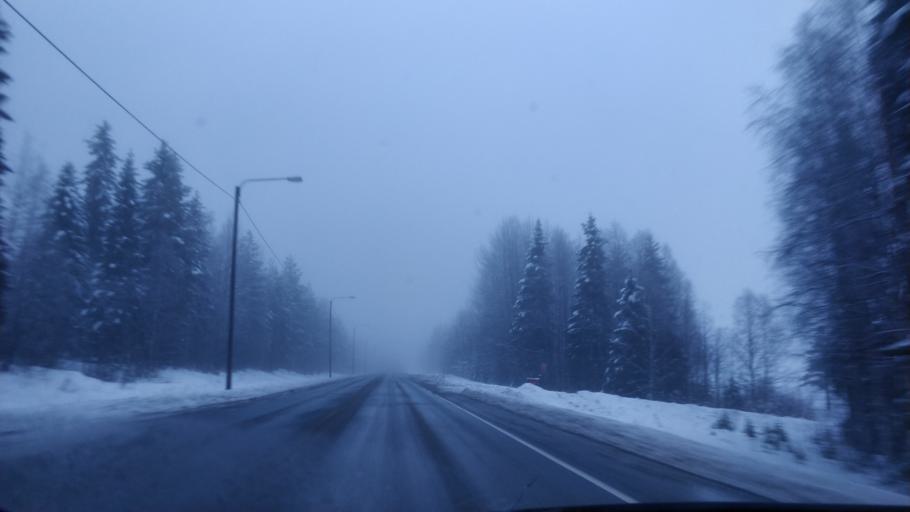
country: FI
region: Lapland
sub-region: Kemi-Tornio
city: Tervola
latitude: 66.1315
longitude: 24.8995
